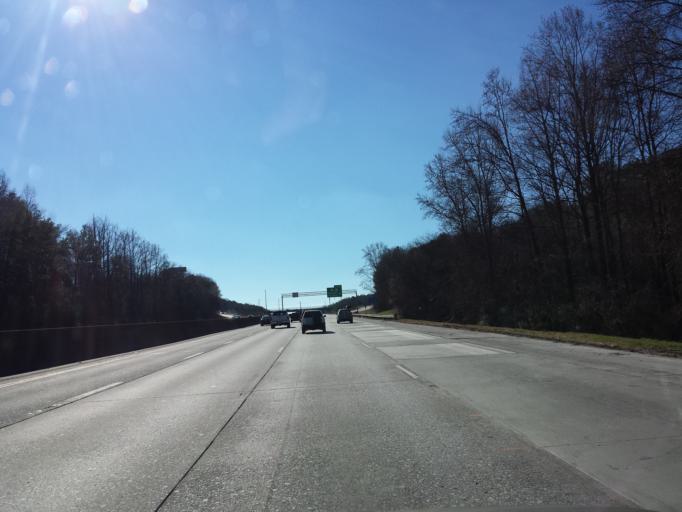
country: US
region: Georgia
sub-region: Cobb County
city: Vinings
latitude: 33.7914
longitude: -84.4894
